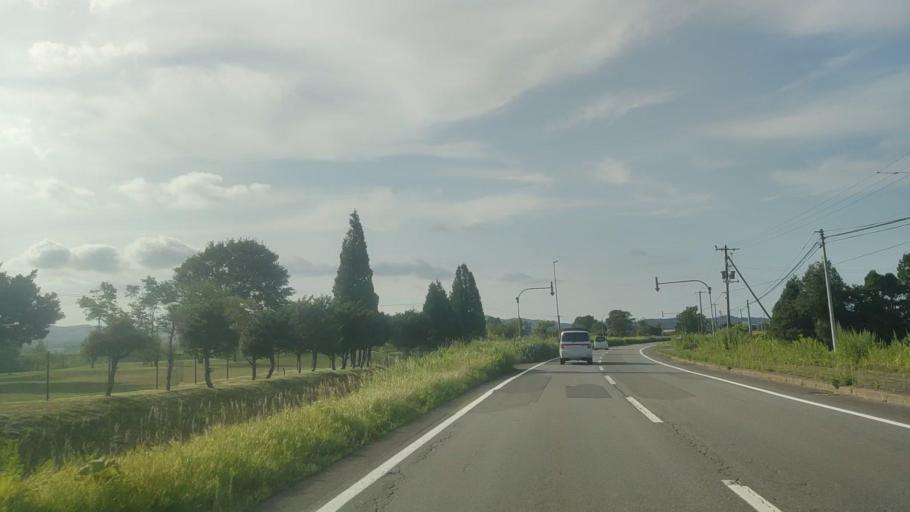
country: JP
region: Hokkaido
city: Chitose
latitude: 42.9541
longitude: 141.7997
